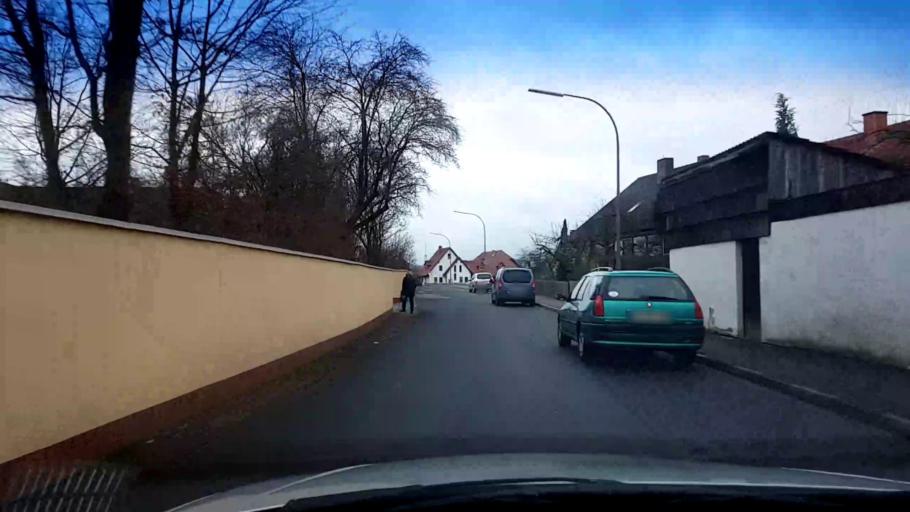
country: DE
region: Bavaria
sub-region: Upper Franconia
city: Oberhaid
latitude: 49.9331
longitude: 10.8218
